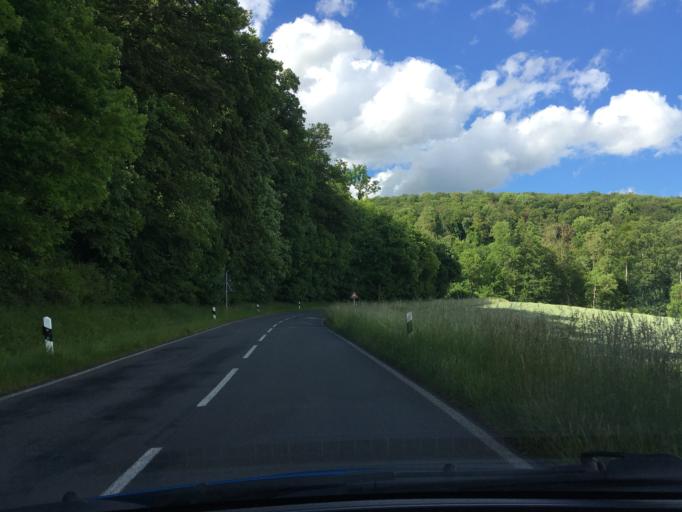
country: DE
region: Lower Saxony
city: Moringen
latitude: 51.7259
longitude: 9.8801
